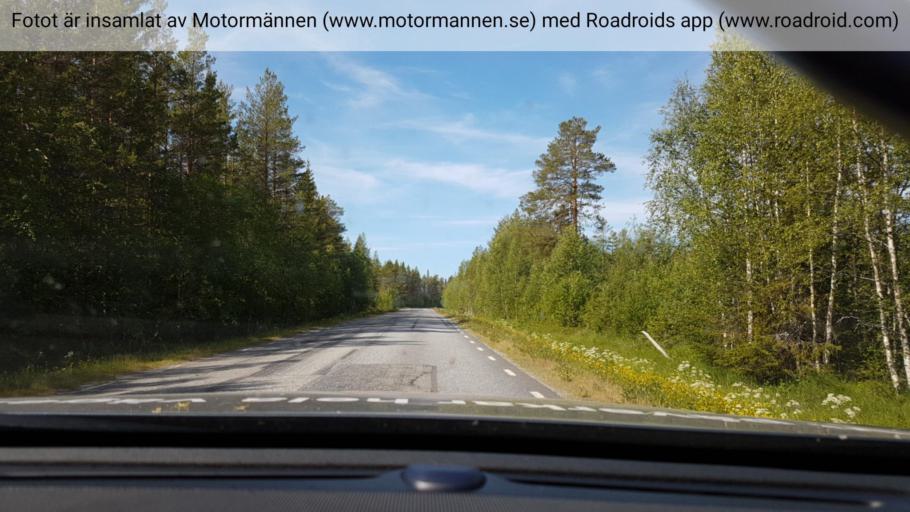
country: SE
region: Vaesterbotten
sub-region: Dorotea Kommun
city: Dorotea
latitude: 64.3683
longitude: 16.1673
